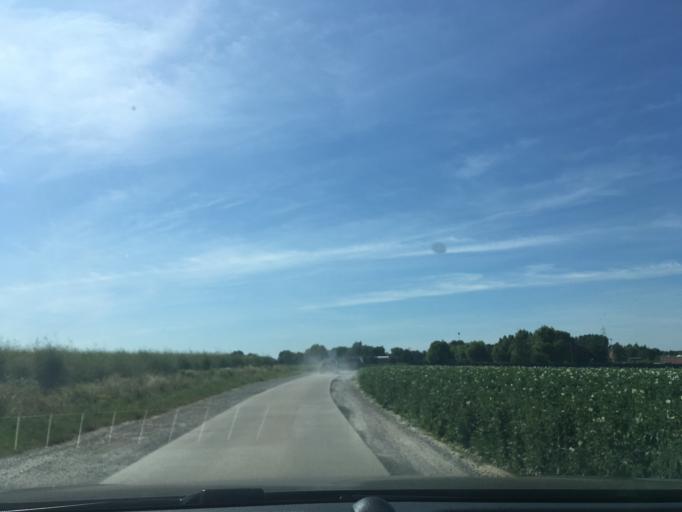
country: BE
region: Flanders
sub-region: Provincie West-Vlaanderen
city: Tielt
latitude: 50.9763
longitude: 3.3181
